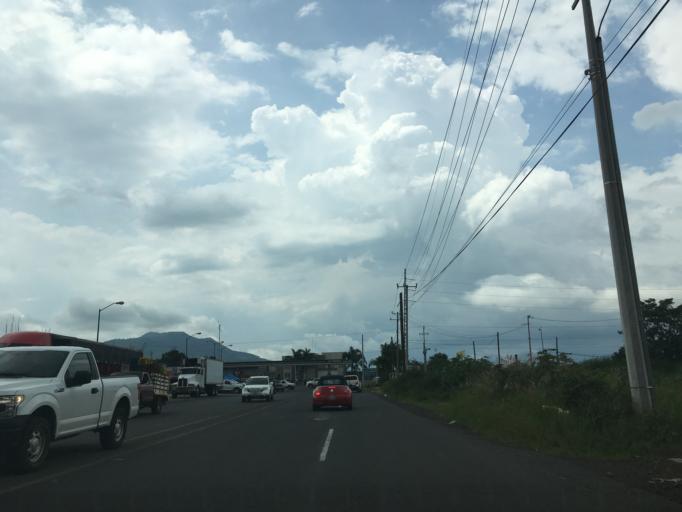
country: MX
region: Michoacan
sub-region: Periban
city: Gildardo Magana (Los Angeles)
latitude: 19.5771
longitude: -102.4776
